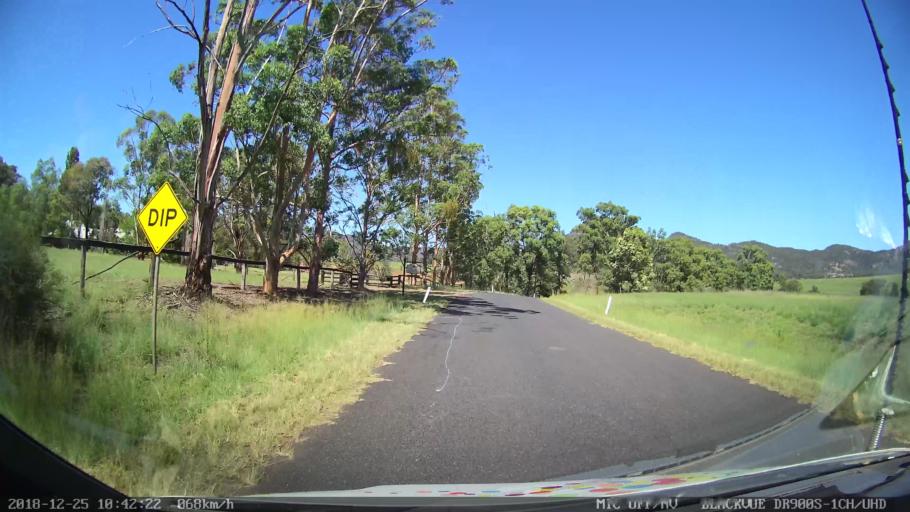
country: AU
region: New South Wales
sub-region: Upper Hunter Shire
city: Merriwa
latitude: -32.4159
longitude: 150.3241
